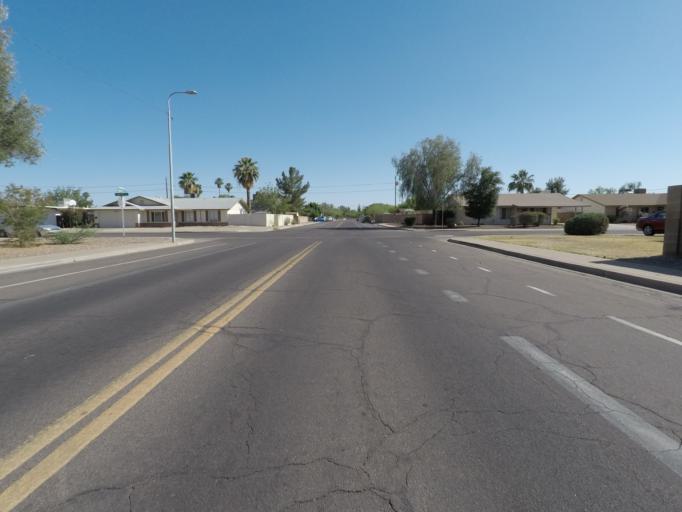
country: US
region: Arizona
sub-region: Maricopa County
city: Tempe
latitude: 33.3986
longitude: -111.9163
